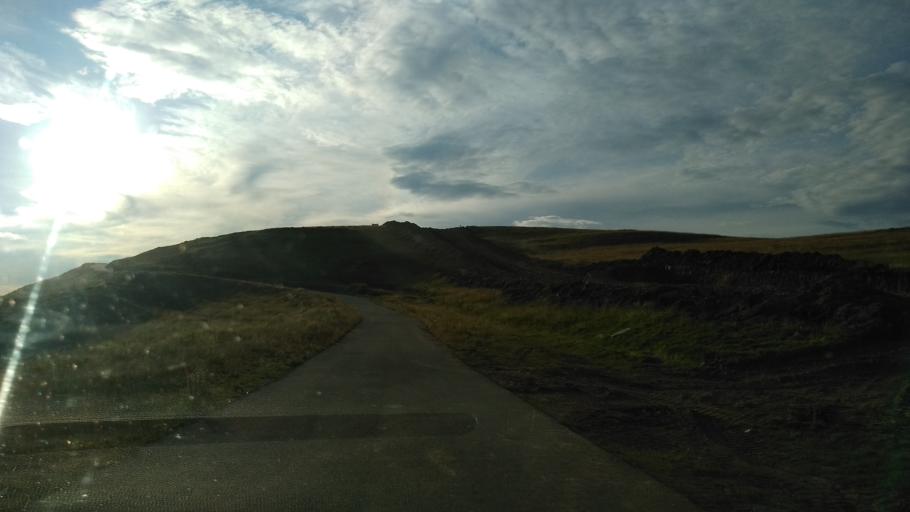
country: RO
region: Hunedoara
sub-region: Municipiul  Vulcan
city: Jiu-Paroseni
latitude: 45.3096
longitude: 23.3122
